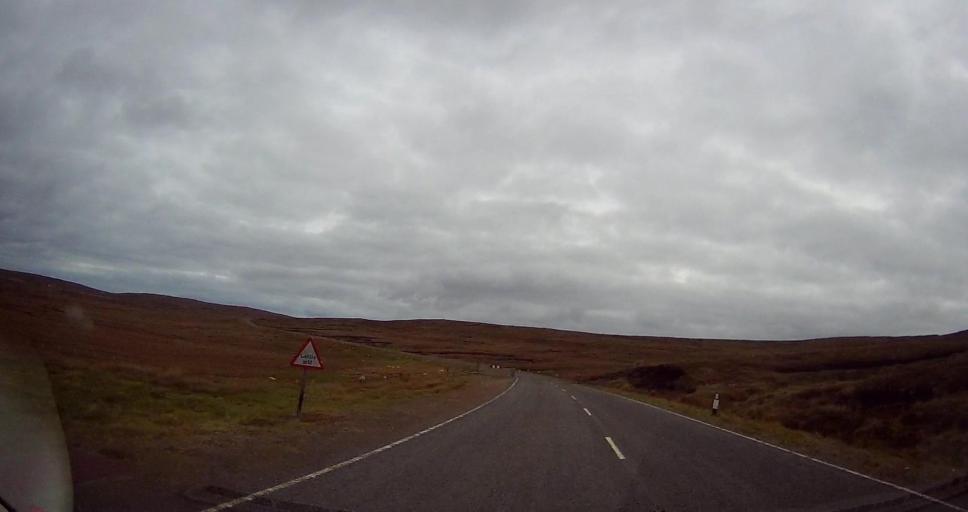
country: GB
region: Scotland
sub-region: Shetland Islands
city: Shetland
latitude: 60.6457
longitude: -1.0717
